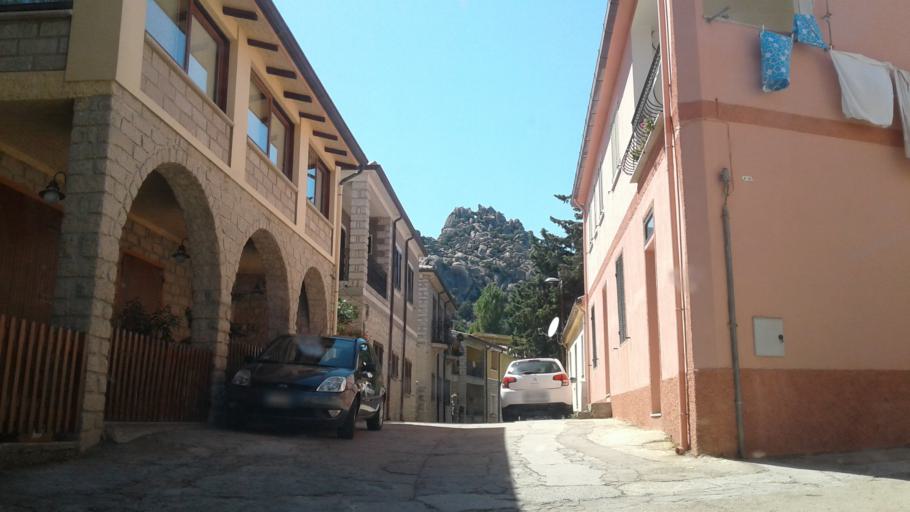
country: IT
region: Sardinia
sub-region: Provincia di Olbia-Tempio
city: Aggius
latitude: 40.9312
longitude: 9.0675
